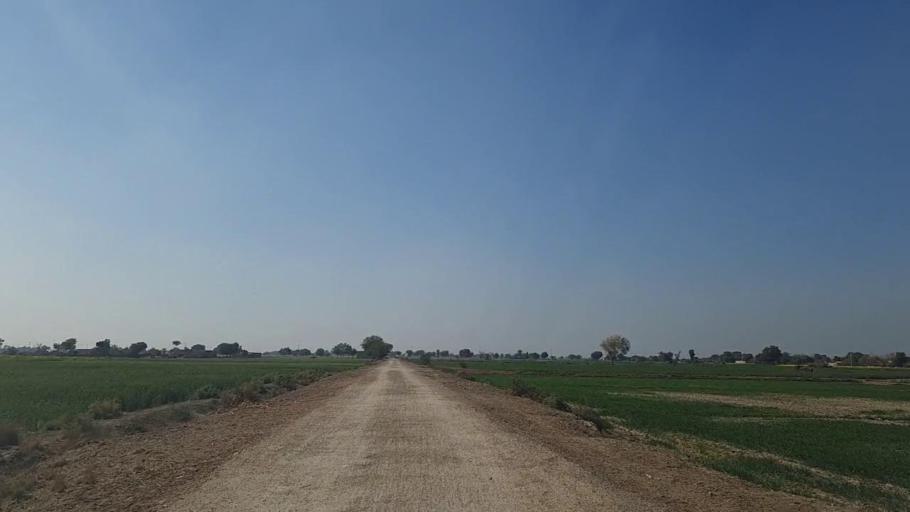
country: PK
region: Sindh
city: Shahpur Chakar
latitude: 26.2143
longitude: 68.5811
